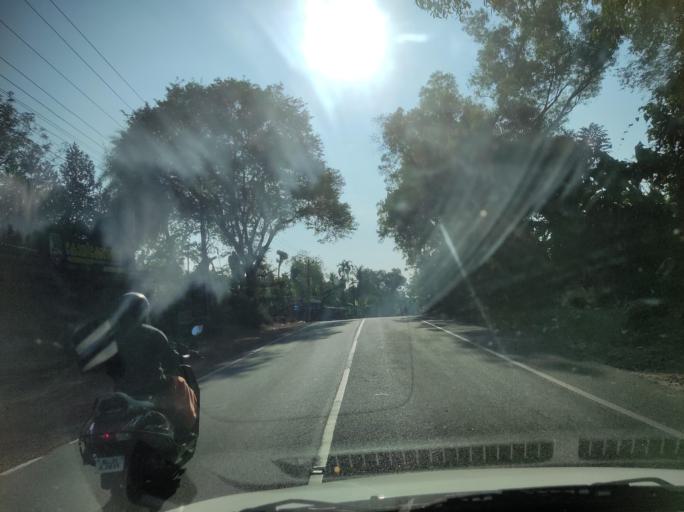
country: IN
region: Kerala
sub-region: Alappuzha
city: Kattanam
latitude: 9.1751
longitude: 76.6269
